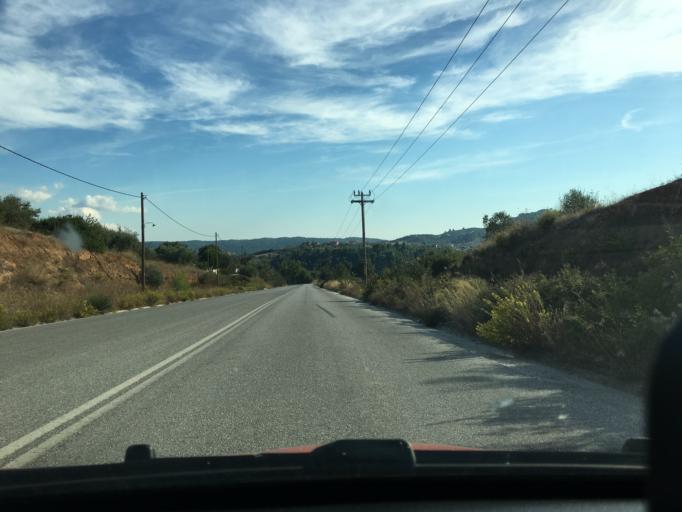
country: GR
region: Central Macedonia
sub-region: Nomos Chalkidikis
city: Agios Nikolaos
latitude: 40.2630
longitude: 23.6985
